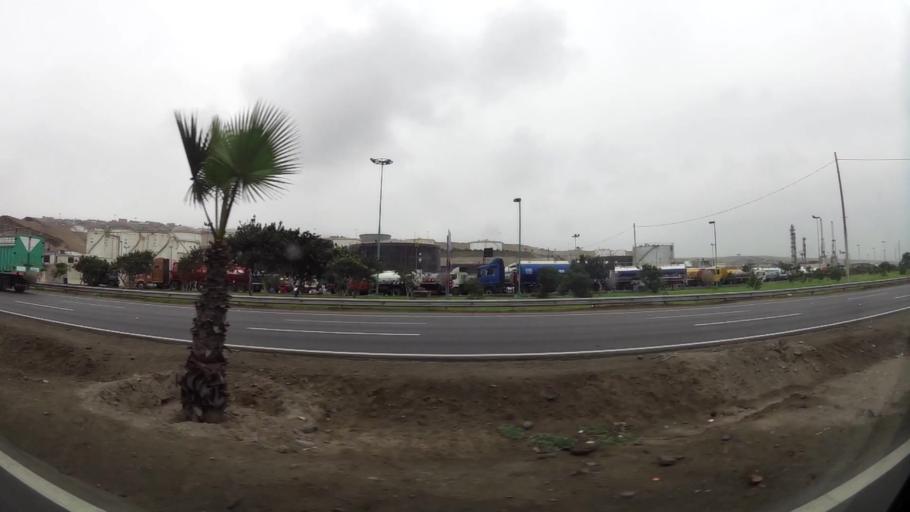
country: PE
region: Lima
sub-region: Lima
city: Punta Hermosa
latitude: -12.2542
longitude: -76.9249
